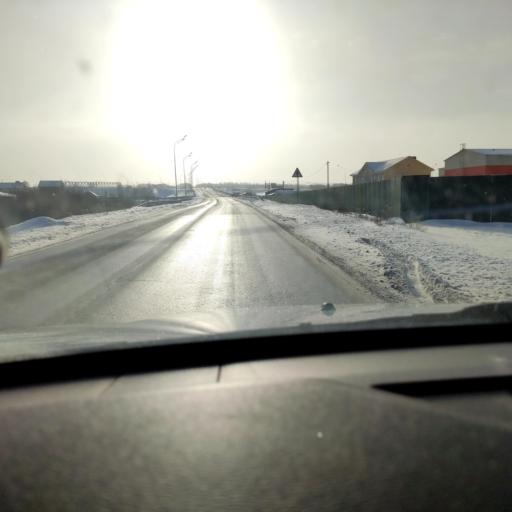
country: RU
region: Samara
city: Smyshlyayevka
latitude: 53.1563
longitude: 50.3846
